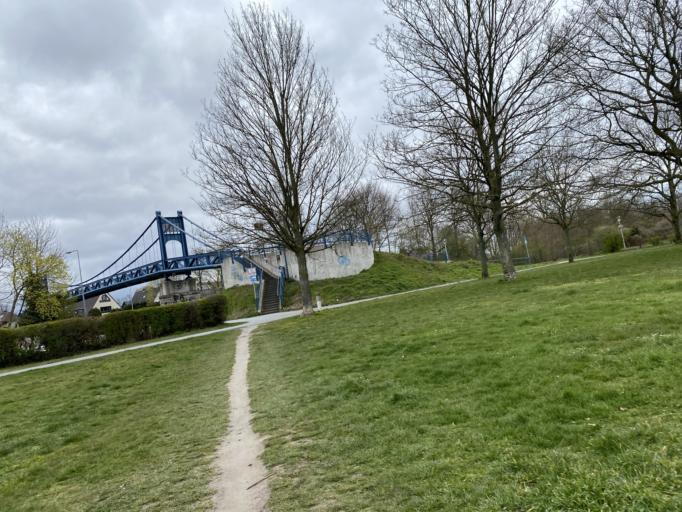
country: DE
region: North Rhine-Westphalia
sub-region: Regierungsbezirk Arnsberg
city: Hamm
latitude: 51.6942
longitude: 7.8697
